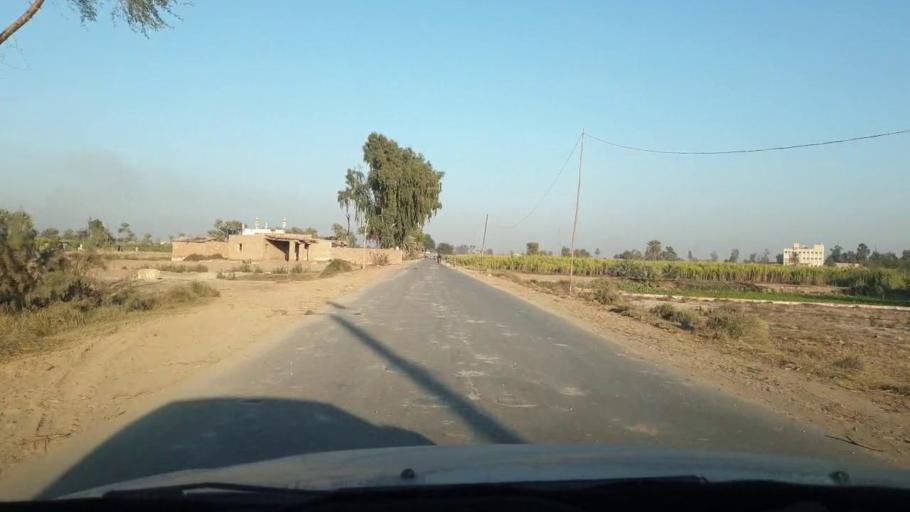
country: PK
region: Sindh
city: Ghotki
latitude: 28.0010
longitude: 69.2917
